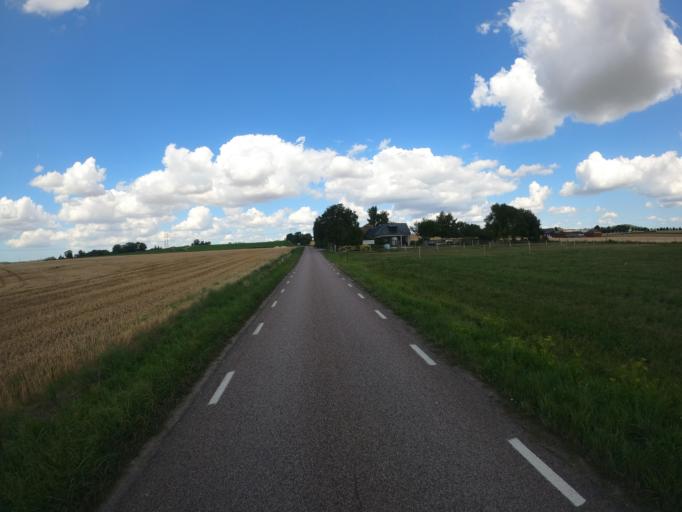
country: SE
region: Skane
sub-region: Staffanstorps Kommun
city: Staffanstorp
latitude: 55.6785
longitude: 13.2901
